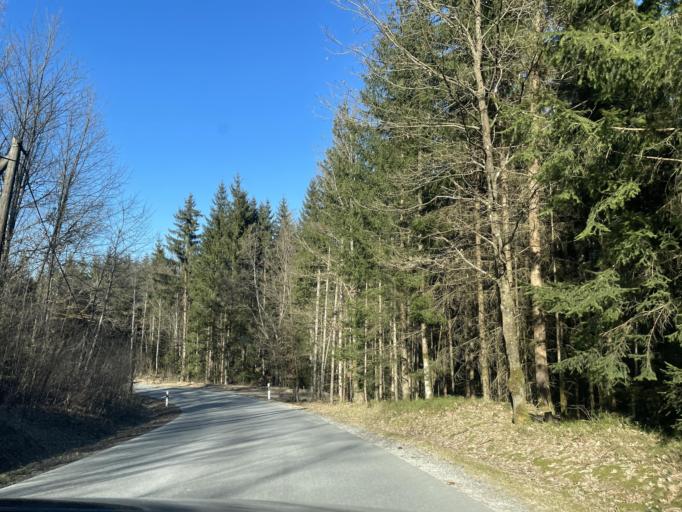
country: DE
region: Bavaria
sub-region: Lower Bavaria
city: Geiersthal
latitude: 49.0748
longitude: 12.9882
